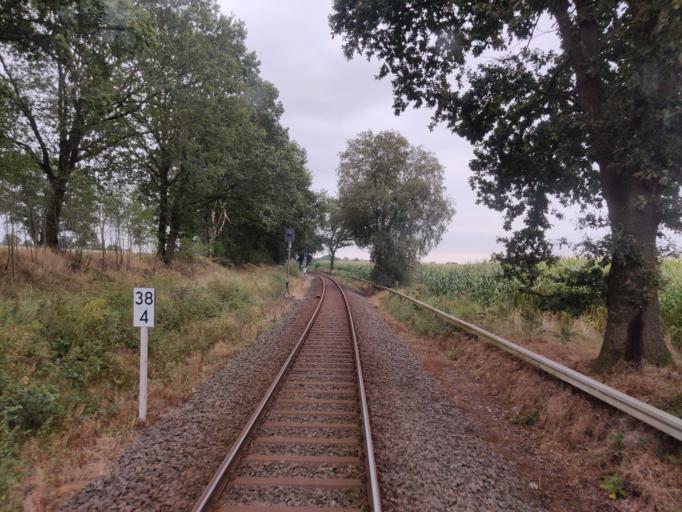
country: DE
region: Lower Saxony
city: Bremervorde
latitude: 53.4731
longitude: 9.1709
